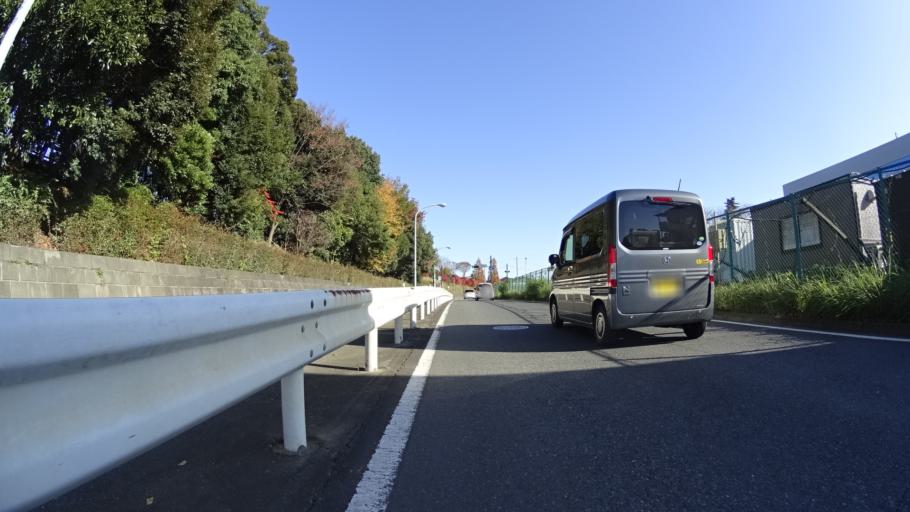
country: JP
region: Tokyo
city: Hino
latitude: 35.6130
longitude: 139.4147
